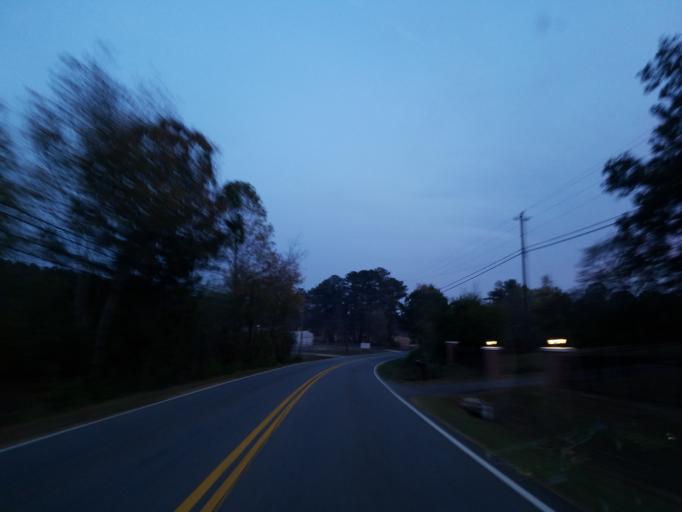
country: US
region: Georgia
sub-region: Pickens County
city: Jasper
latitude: 34.4812
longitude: -84.4499
